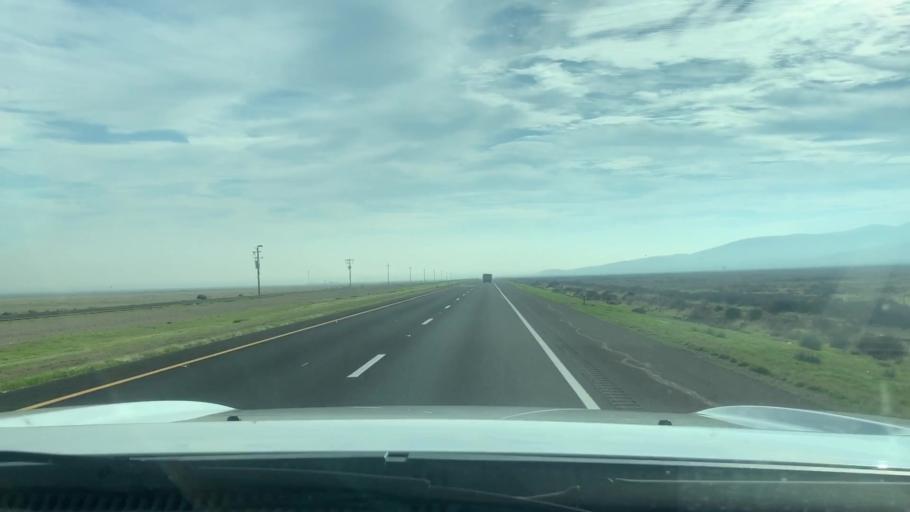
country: US
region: California
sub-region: San Luis Obispo County
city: Shandon
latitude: 35.6666
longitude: -120.0730
